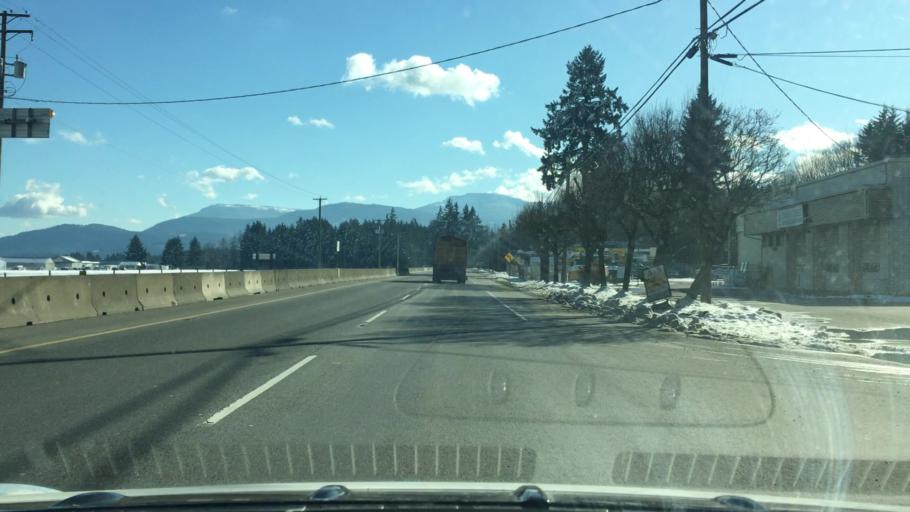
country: CA
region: British Columbia
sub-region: Cowichan Valley Regional District
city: Ladysmith
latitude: 49.0528
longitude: -123.8776
